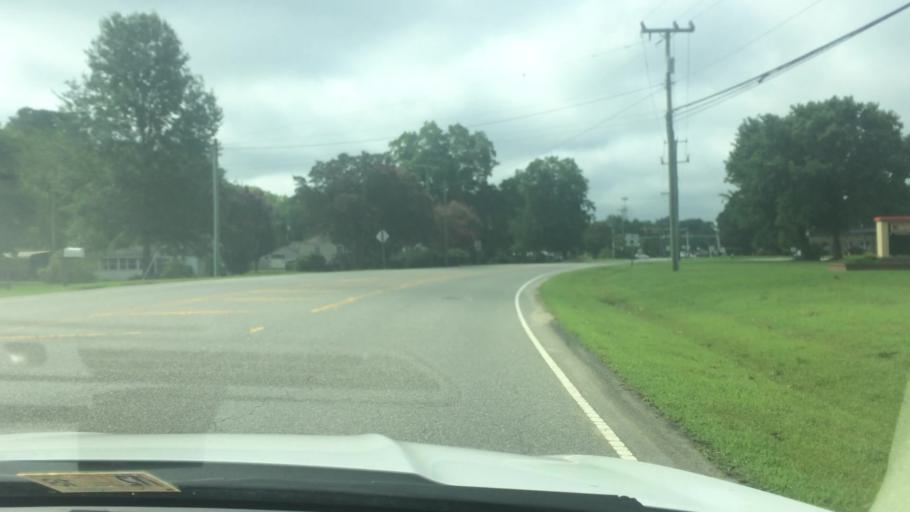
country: US
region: Virginia
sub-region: City of Poquoson
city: Poquoson
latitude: 37.1244
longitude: -76.4330
